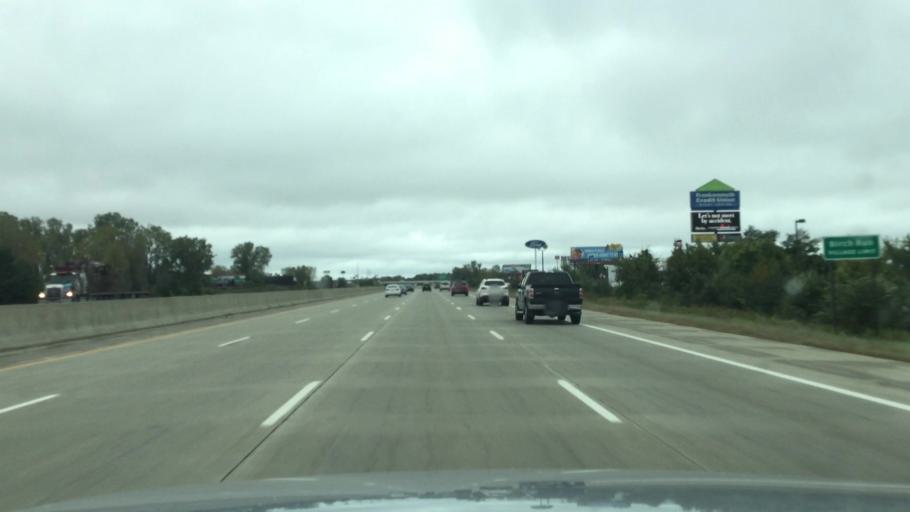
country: US
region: Michigan
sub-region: Saginaw County
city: Birch Run
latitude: 43.2575
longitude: -83.7829
